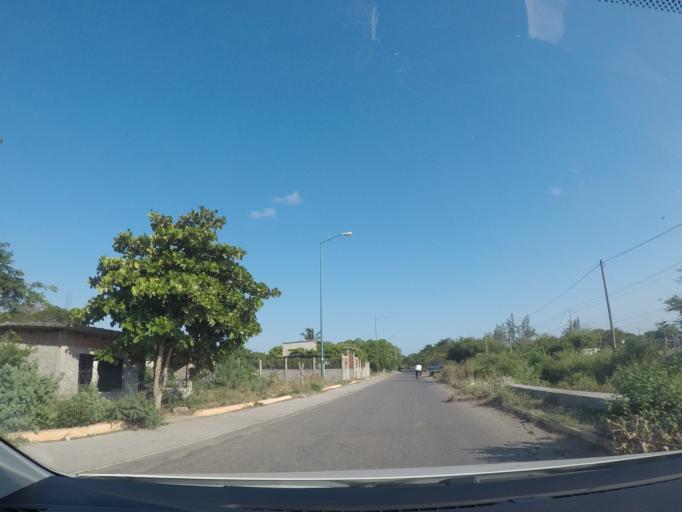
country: MX
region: Oaxaca
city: Juchitan de Zaragoza
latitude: 16.4184
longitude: -95.0267
